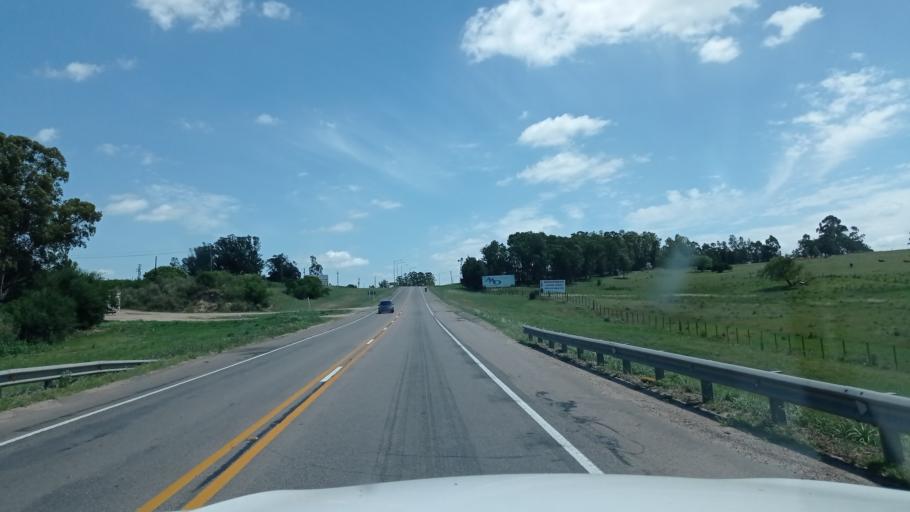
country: UY
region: Florida
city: Florida
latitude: -34.1253
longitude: -56.1883
